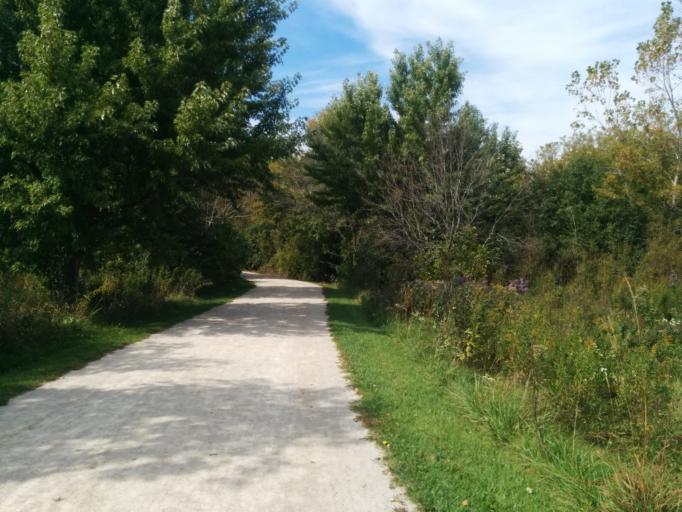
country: US
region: Illinois
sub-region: DuPage County
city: Carol Stream
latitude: 41.9426
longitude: -88.1784
